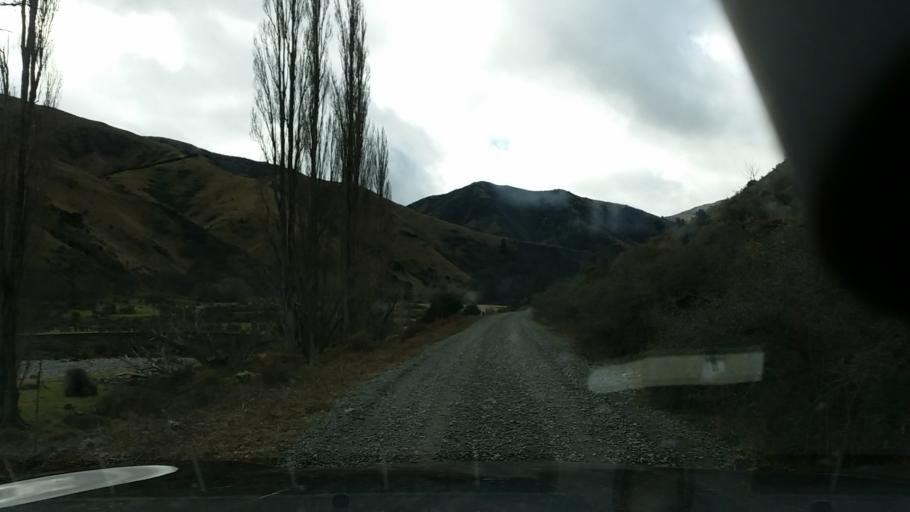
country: NZ
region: Tasman
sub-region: Tasman District
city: Brightwater
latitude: -41.7432
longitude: 173.4144
